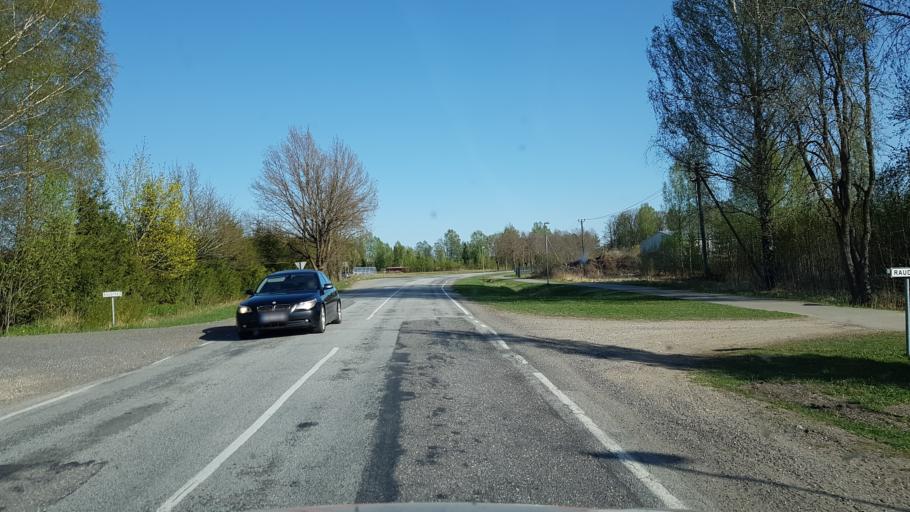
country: EE
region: Paernumaa
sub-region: Paikuse vald
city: Paikuse
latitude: 58.3749
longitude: 24.6250
